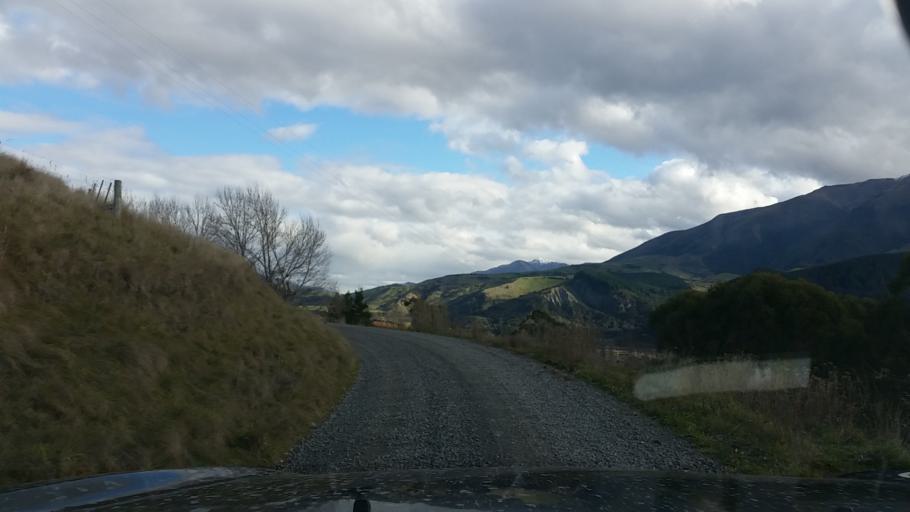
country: NZ
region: Marlborough
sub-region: Marlborough District
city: Blenheim
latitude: -41.7658
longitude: 173.8584
